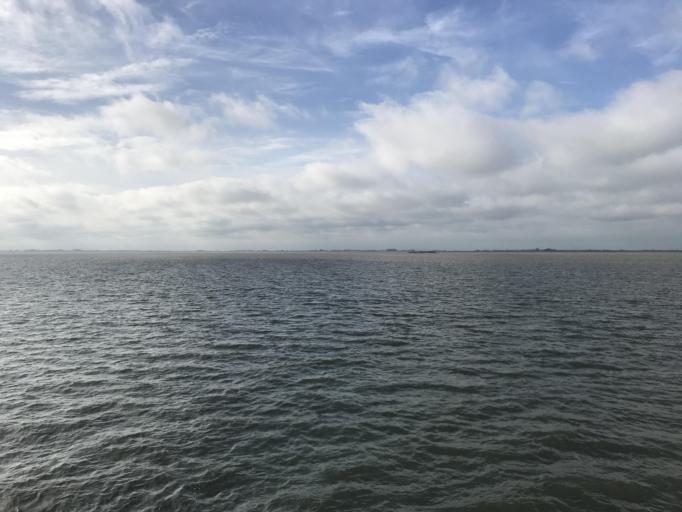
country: NL
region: Groningen
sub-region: Gemeente Delfzijl
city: Delfzijl
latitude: 53.4105
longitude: 6.9418
